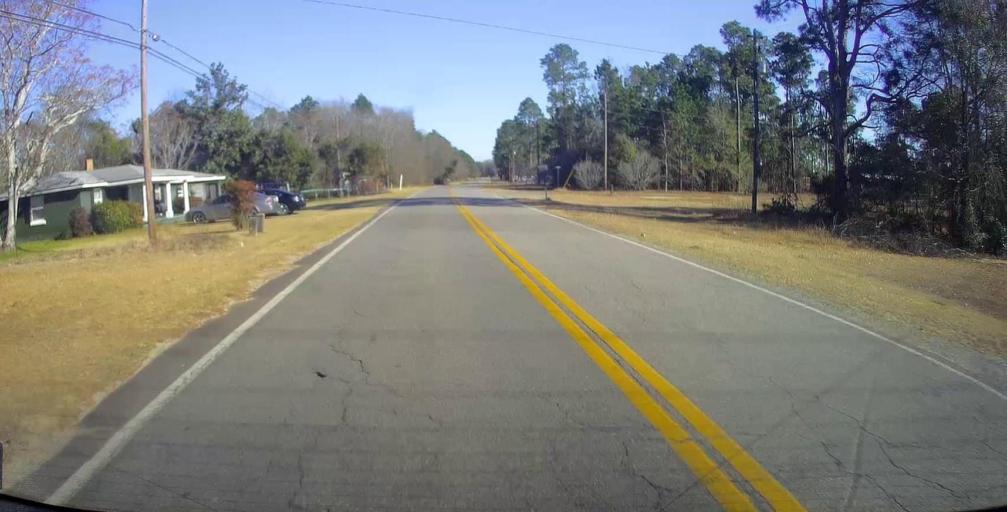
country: US
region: Georgia
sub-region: Taylor County
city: Butler
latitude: 32.5623
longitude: -84.2529
